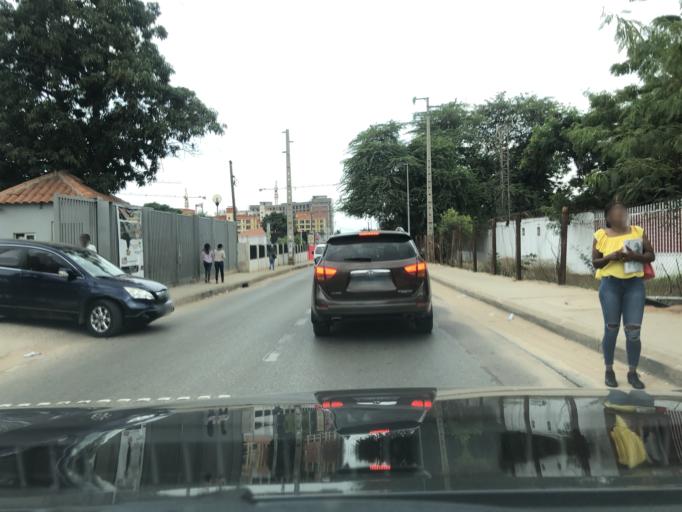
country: AO
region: Luanda
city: Luanda
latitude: -8.8986
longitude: 13.2021
